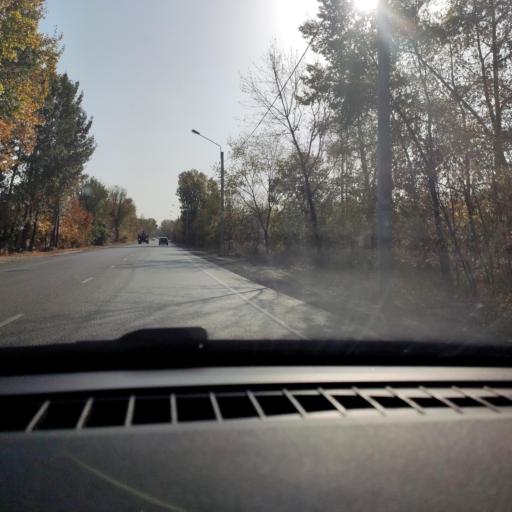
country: RU
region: Voronezj
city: Voronezh
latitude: 51.6051
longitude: 39.1785
